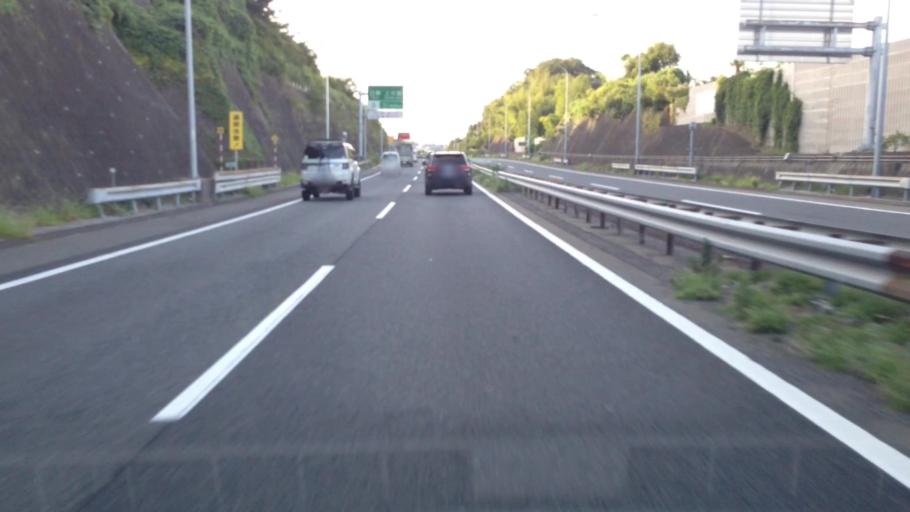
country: JP
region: Kanagawa
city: Kamakura
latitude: 35.3767
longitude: 139.5883
